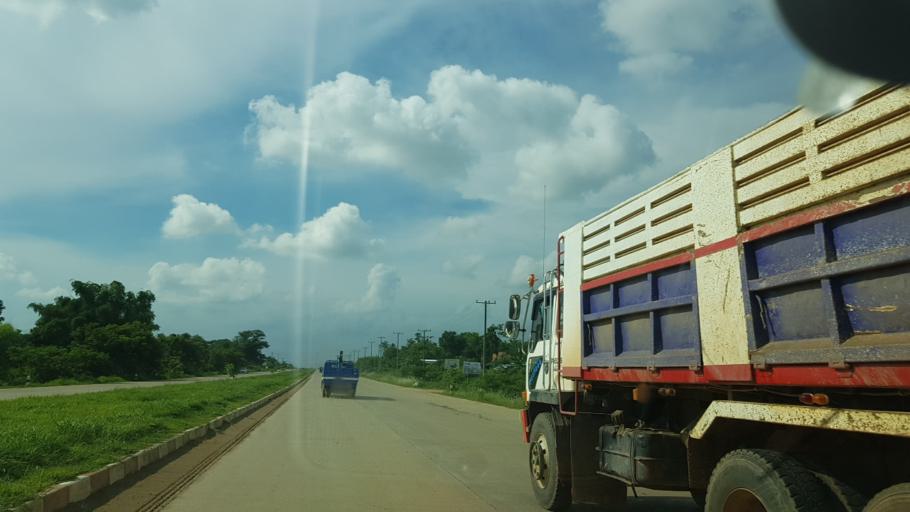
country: TH
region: Nong Khai
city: Nong Khai
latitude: 17.9075
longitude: 102.7202
